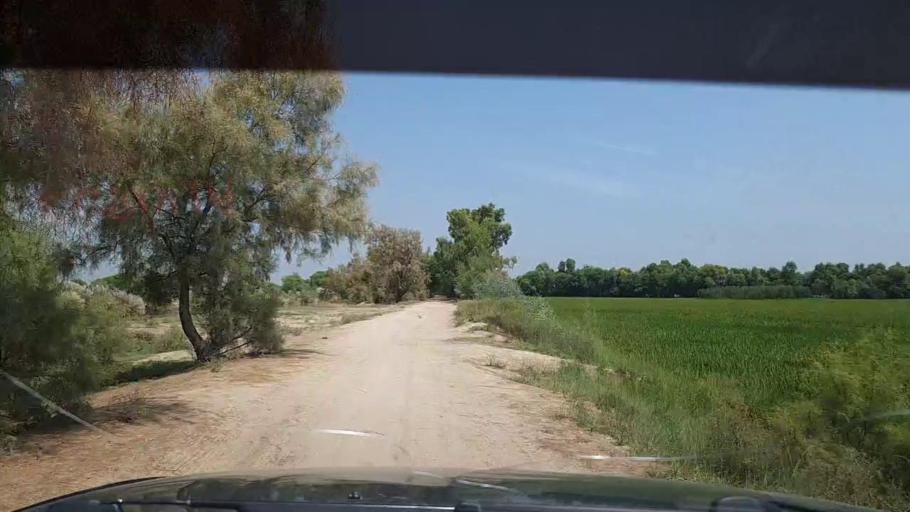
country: PK
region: Sindh
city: Tangwani
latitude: 28.2331
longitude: 68.9671
